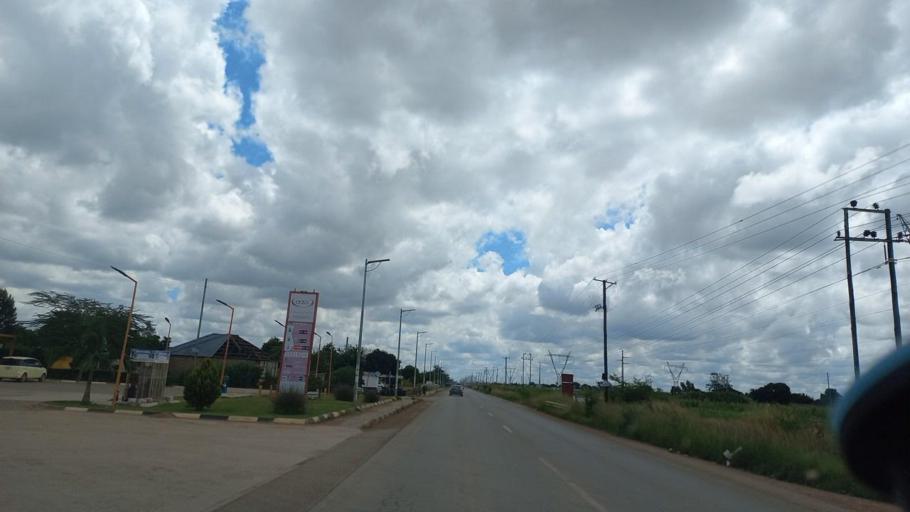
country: ZM
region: Lusaka
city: Lusaka
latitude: -15.4592
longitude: 28.3338
